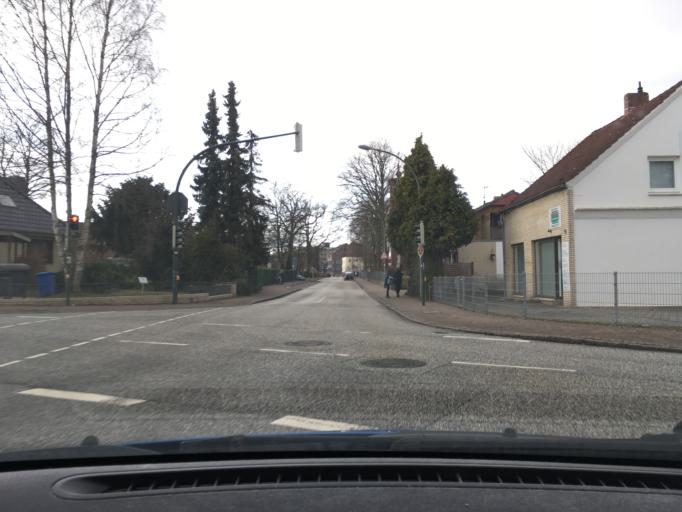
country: DE
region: Schleswig-Holstein
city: Wedel
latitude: 53.5767
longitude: 9.7099
